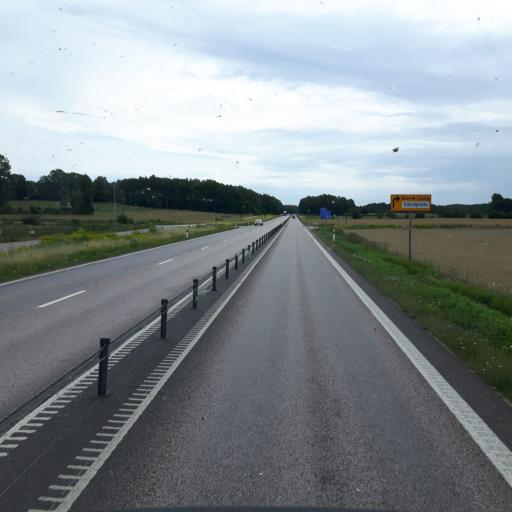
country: SE
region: Skane
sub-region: Hassleholms Kommun
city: Vinslov
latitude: 56.1078
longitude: 13.8692
